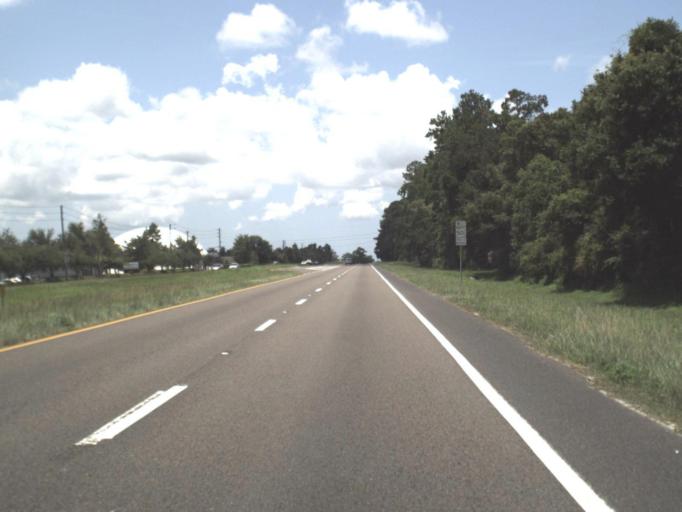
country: US
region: Florida
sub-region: Hernando County
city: South Brooksville
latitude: 28.5384
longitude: -82.3895
